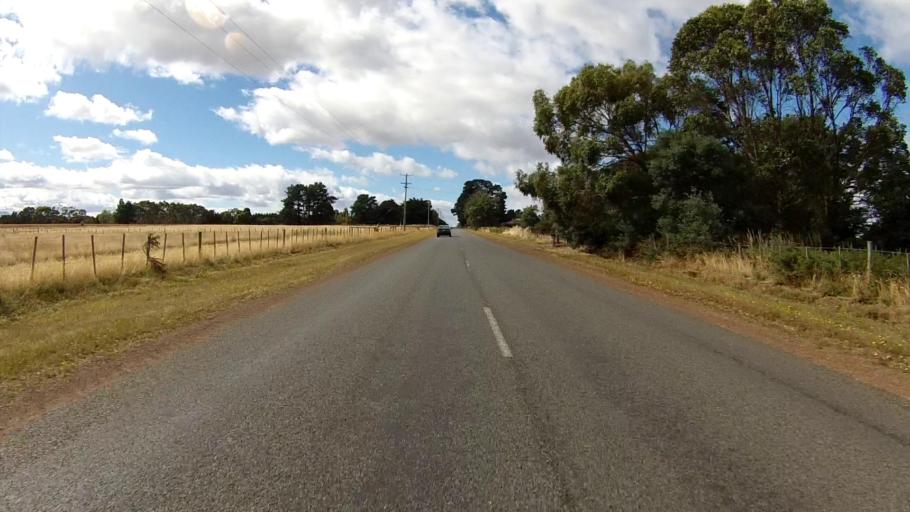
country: AU
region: Tasmania
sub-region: Northern Midlands
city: Evandale
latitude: -41.6039
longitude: 147.2799
